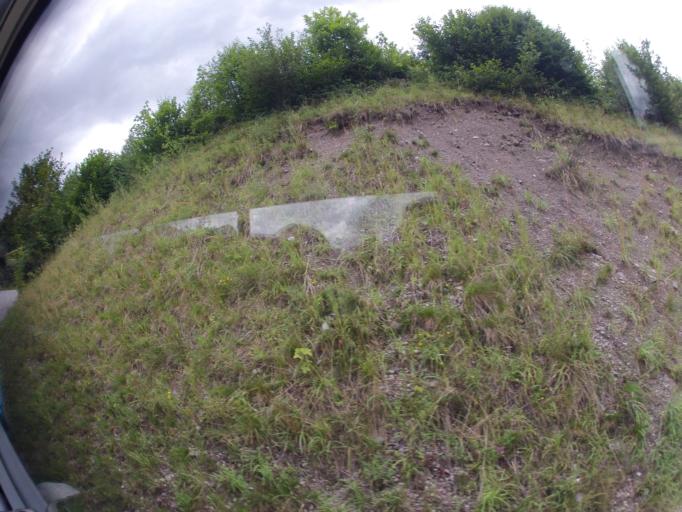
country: AT
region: Salzburg
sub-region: Politischer Bezirk Sankt Johann im Pongau
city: Werfen
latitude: 47.4879
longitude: 13.1973
